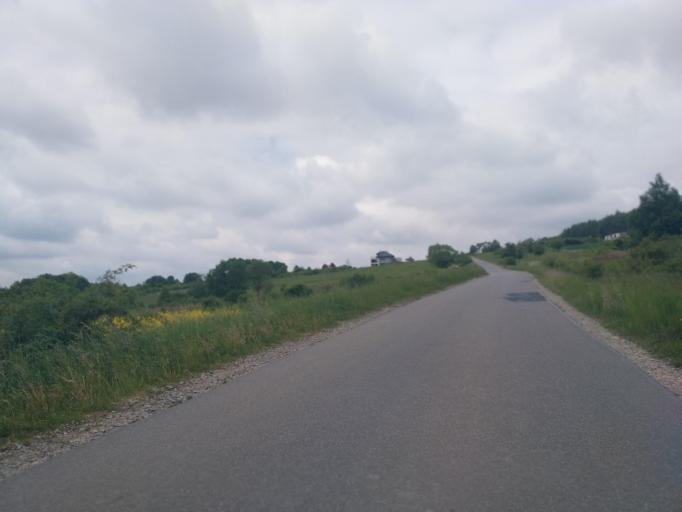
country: PL
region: Subcarpathian Voivodeship
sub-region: Powiat krosnienski
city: Chorkowka
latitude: 49.6707
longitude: 21.6708
